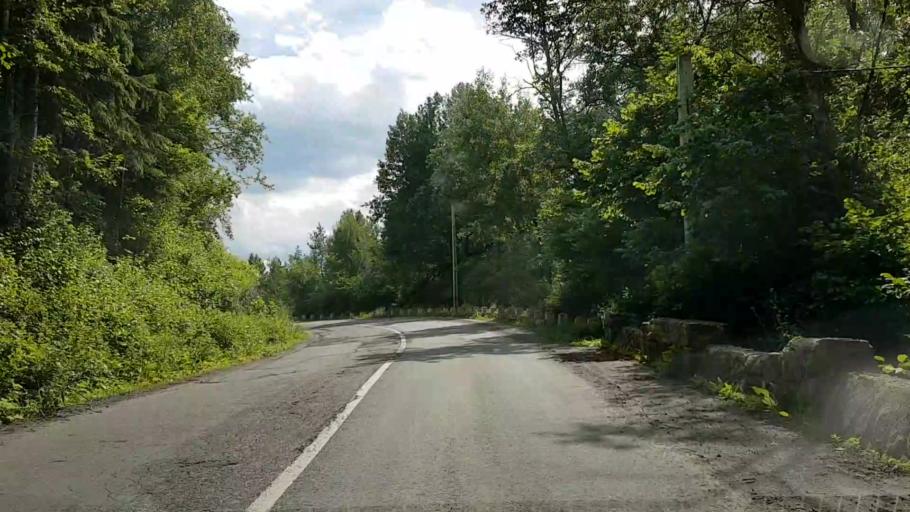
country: RO
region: Neamt
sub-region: Comuna Poiana Teiului
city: Poiana Teiului
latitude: 47.0754
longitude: 25.9643
